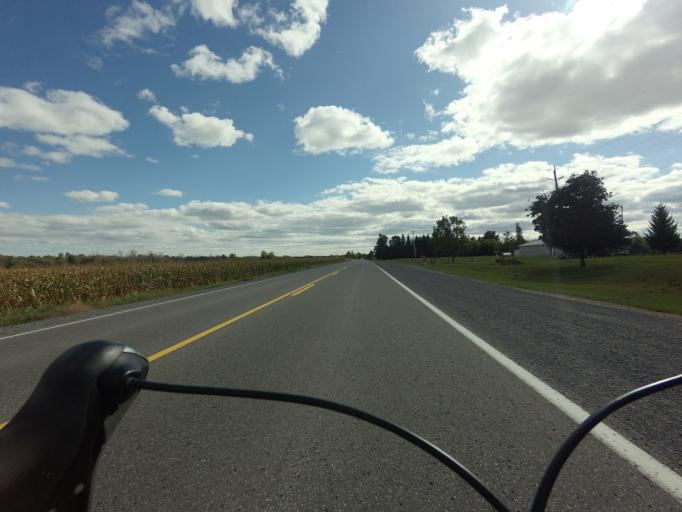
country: CA
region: Ontario
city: Bells Corners
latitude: 45.1648
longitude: -75.6560
